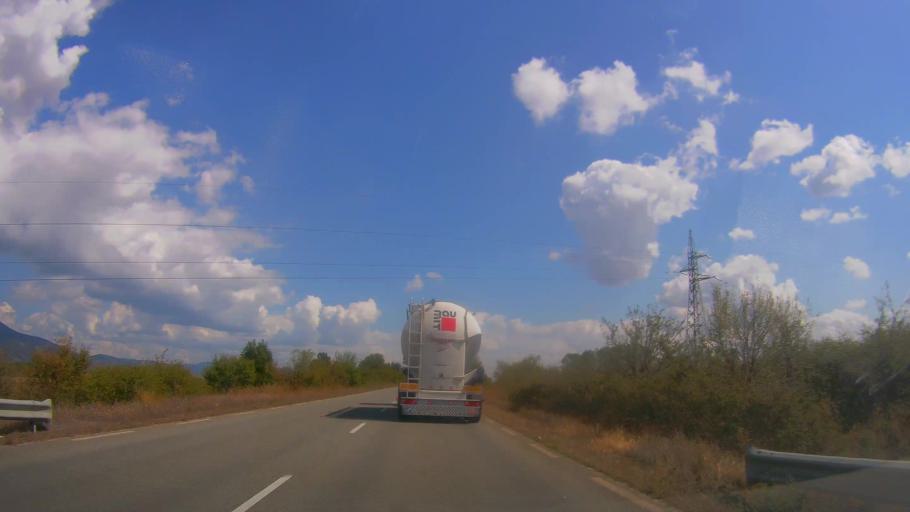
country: BG
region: Sliven
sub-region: Obshtina Tvurditsa
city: Tvurditsa
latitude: 42.6570
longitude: 25.9225
